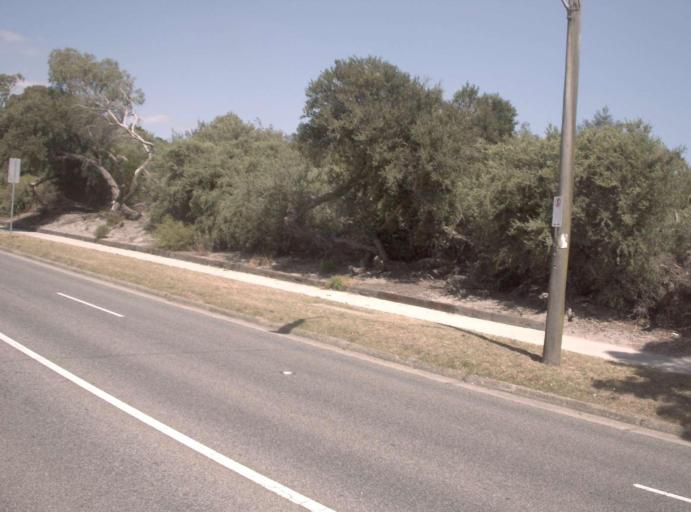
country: AU
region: Victoria
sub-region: Bayside
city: Highett
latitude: -37.9545
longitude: 145.0275
